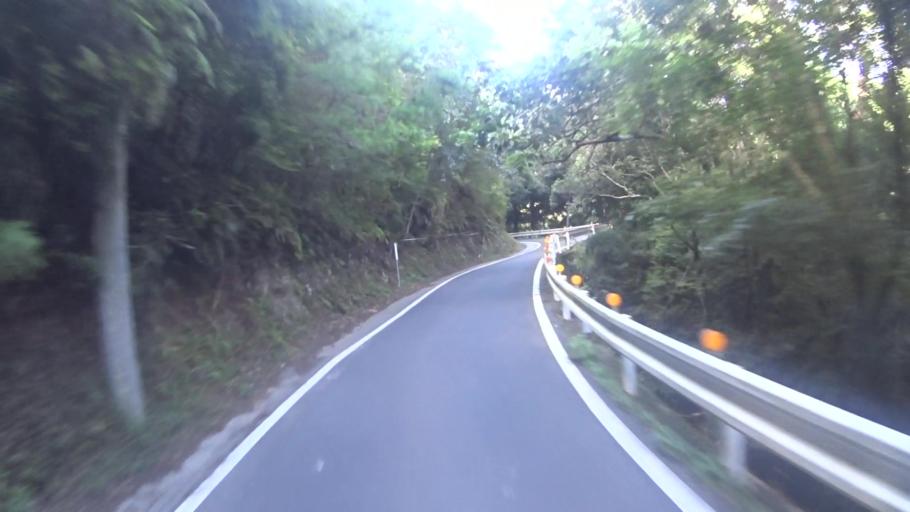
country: JP
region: Kyoto
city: Uji
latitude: 34.8087
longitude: 135.8925
